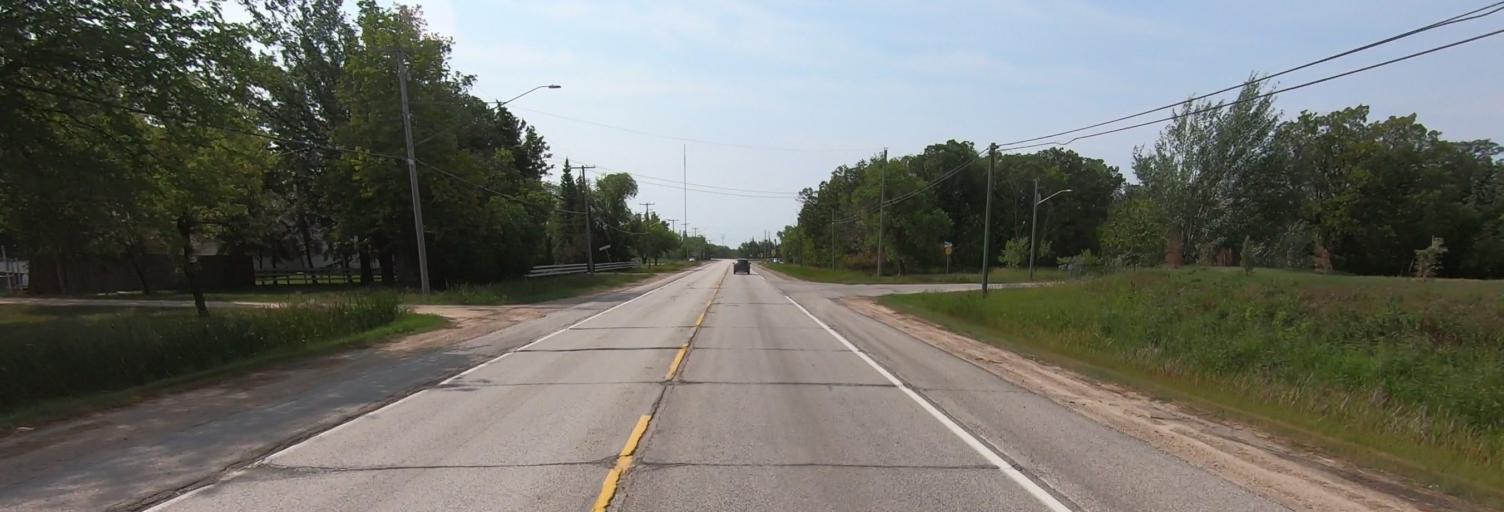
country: CA
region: Manitoba
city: Winnipeg
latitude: 49.7718
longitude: -97.1276
